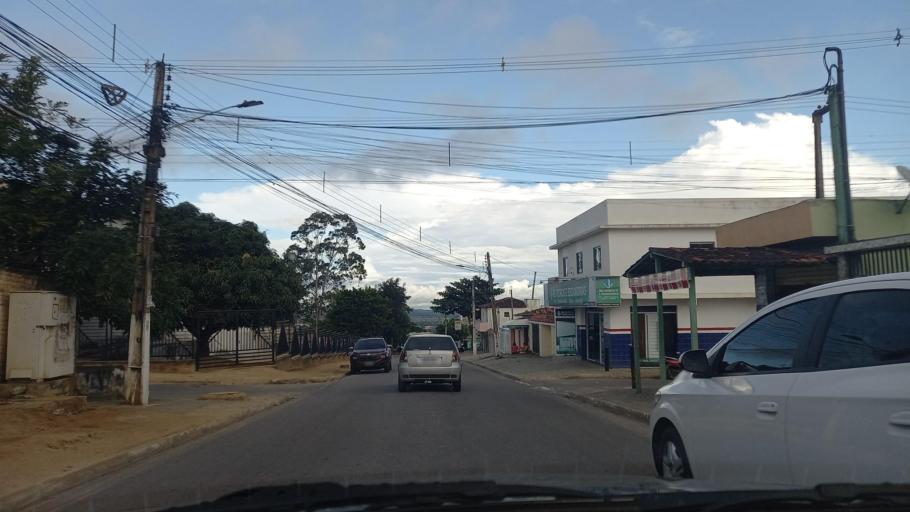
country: BR
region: Pernambuco
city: Garanhuns
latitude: -8.9045
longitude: -36.4905
